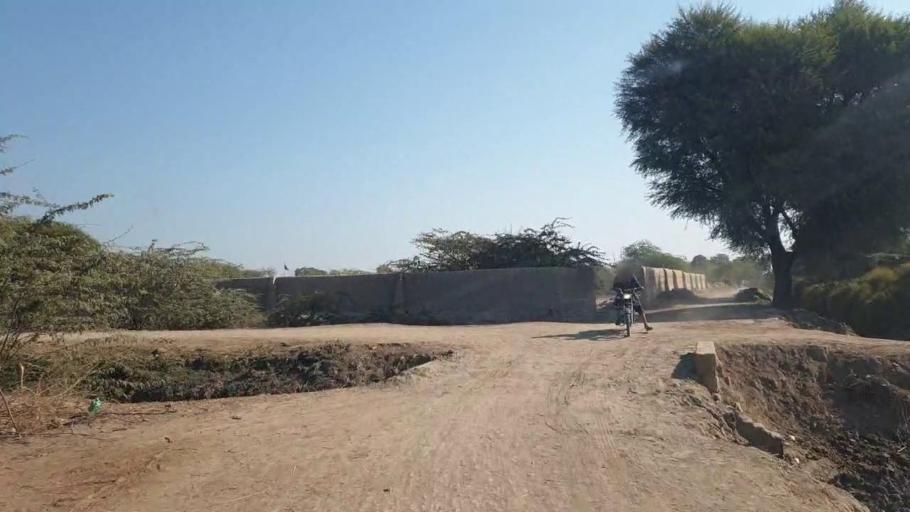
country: PK
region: Sindh
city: Shahpur Chakar
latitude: 26.0819
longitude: 68.6047
